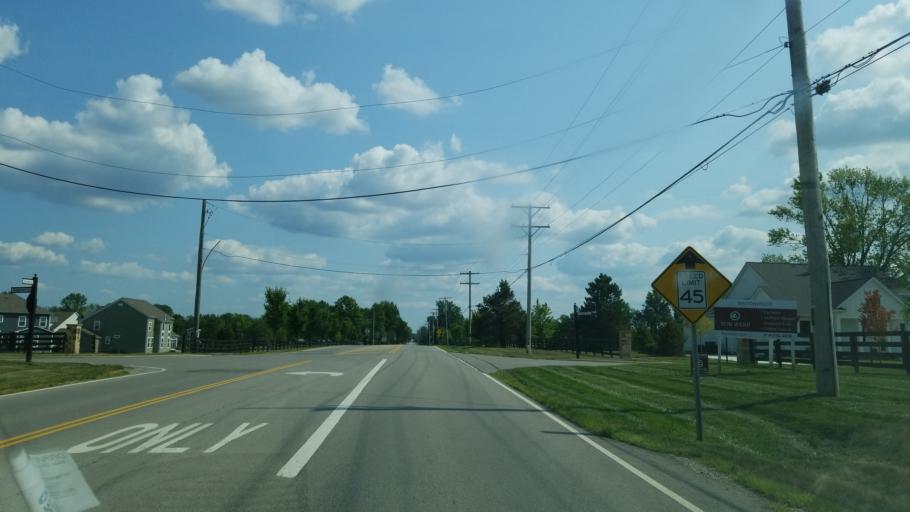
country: US
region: Ohio
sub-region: Union County
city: New California
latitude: 40.1733
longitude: -83.1768
